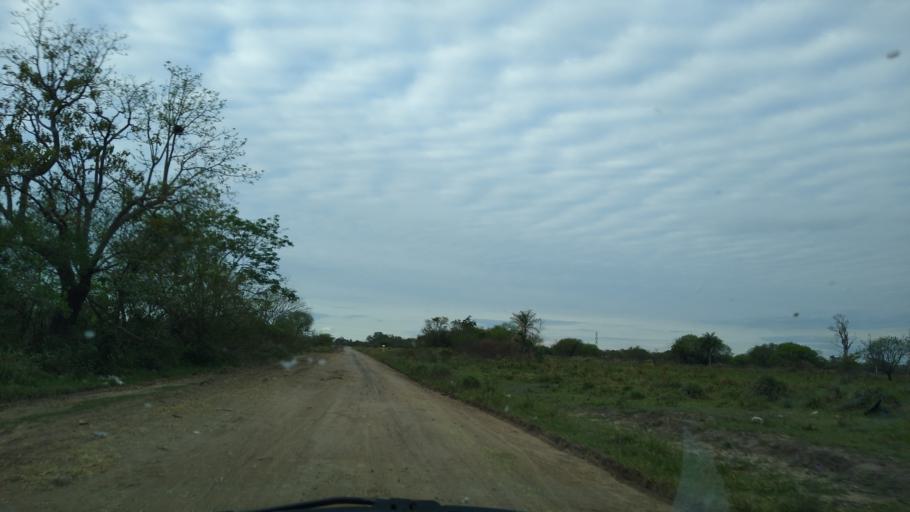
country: AR
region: Chaco
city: Puerto Tirol
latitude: -27.3904
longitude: -59.0497
